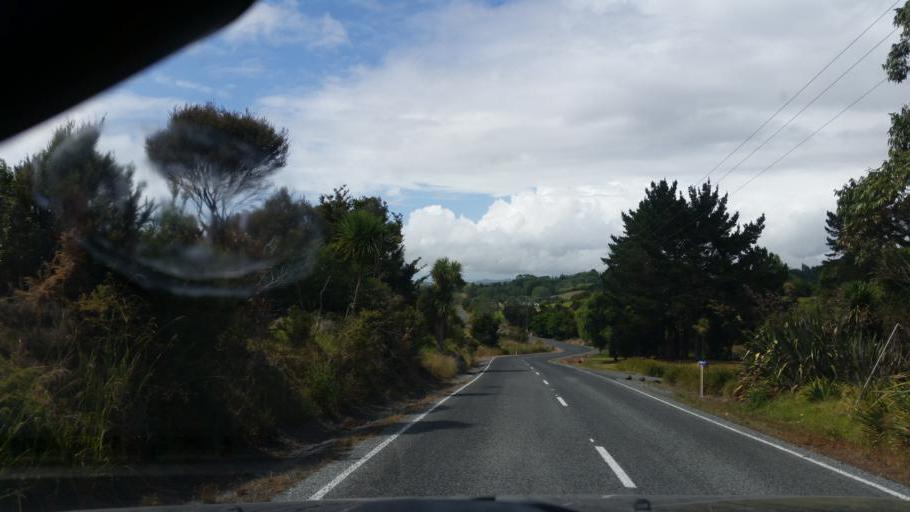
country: NZ
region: Auckland
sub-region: Auckland
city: Wellsford
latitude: -36.1161
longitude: 174.5449
